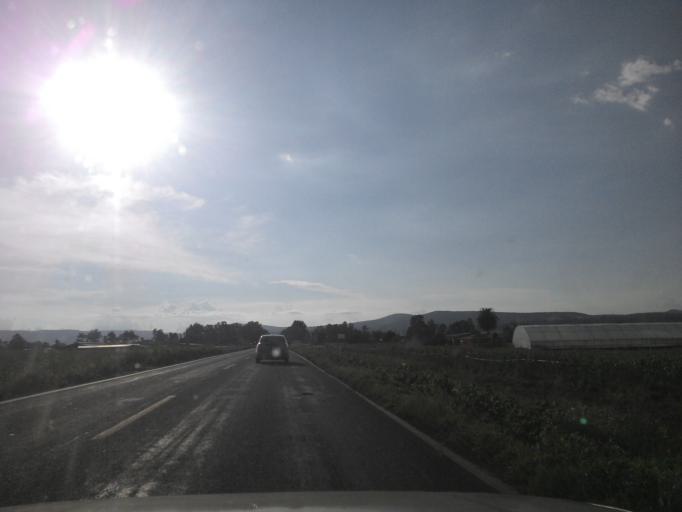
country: MX
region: Jalisco
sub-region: Tototlan
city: Nuevo Refugio de Afuera (Nuevo Refugio)
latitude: 20.5598
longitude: -102.7319
